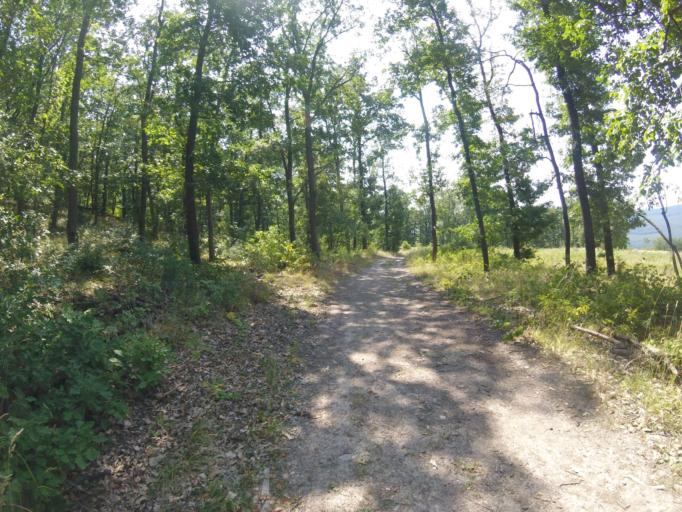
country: HU
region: Pest
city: Csobanka
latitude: 47.6816
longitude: 18.9601
